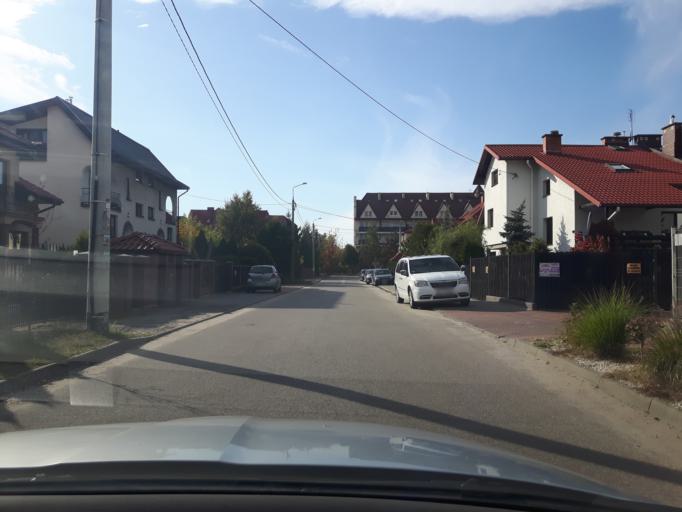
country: PL
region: Masovian Voivodeship
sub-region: Powiat wolominski
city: Zabki
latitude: 52.3054
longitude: 21.1002
